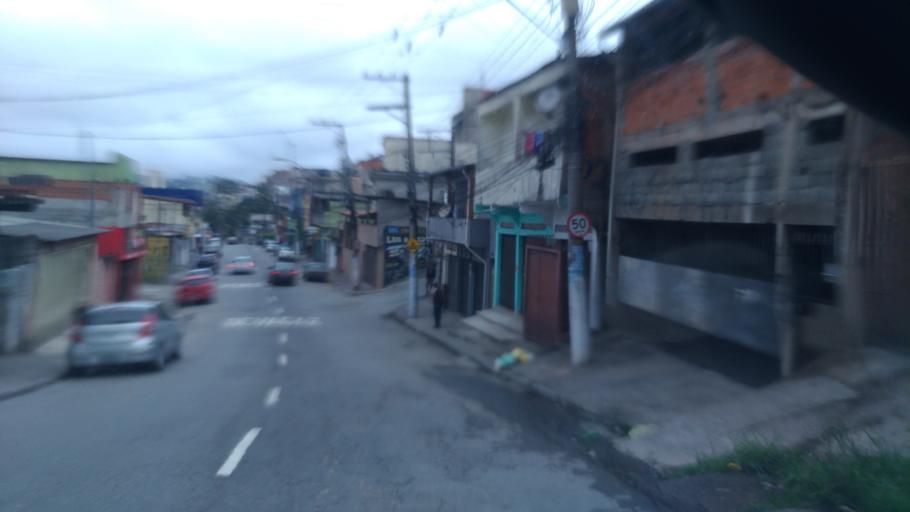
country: BR
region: Sao Paulo
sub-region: Santo Andre
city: Santo Andre
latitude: -23.7039
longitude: -46.5174
